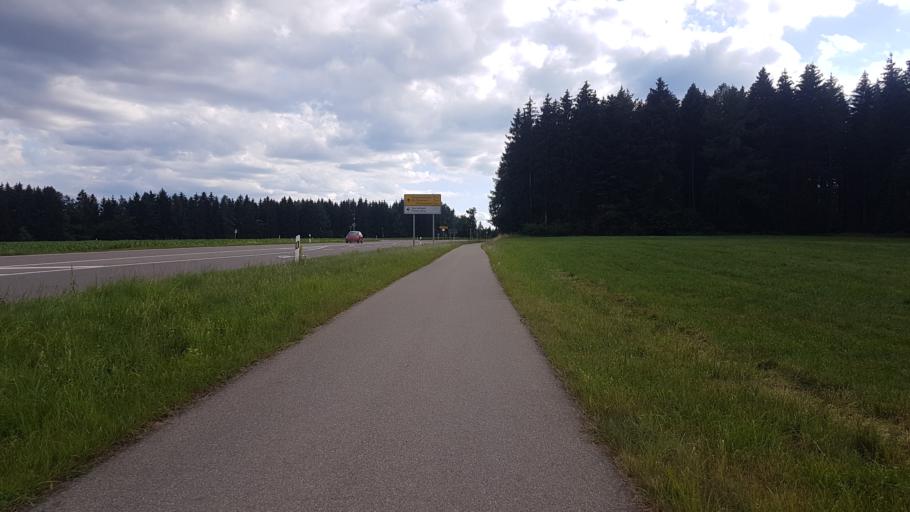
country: DE
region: Baden-Wuerttemberg
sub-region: Freiburg Region
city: Monchweiler
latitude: 48.0466
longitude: 8.4194
